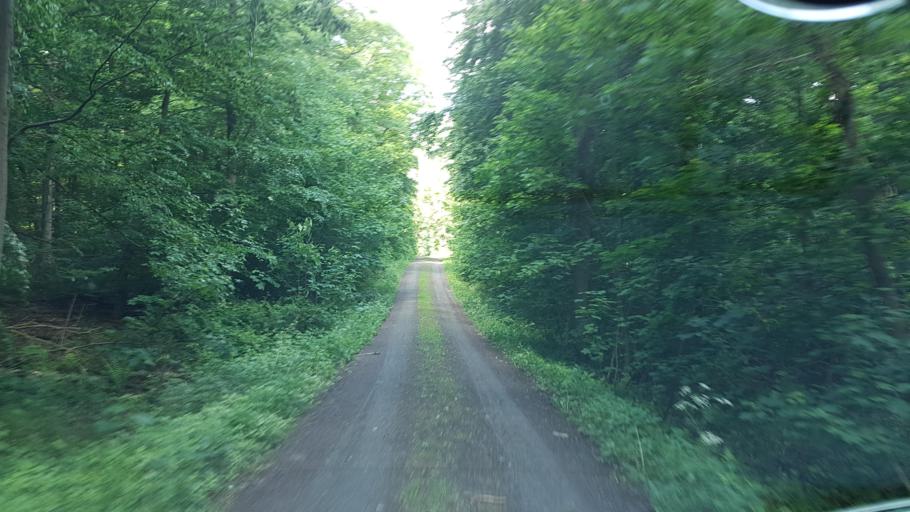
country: DE
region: Lower Saxony
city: Rabke
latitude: 52.1757
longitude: 10.8914
